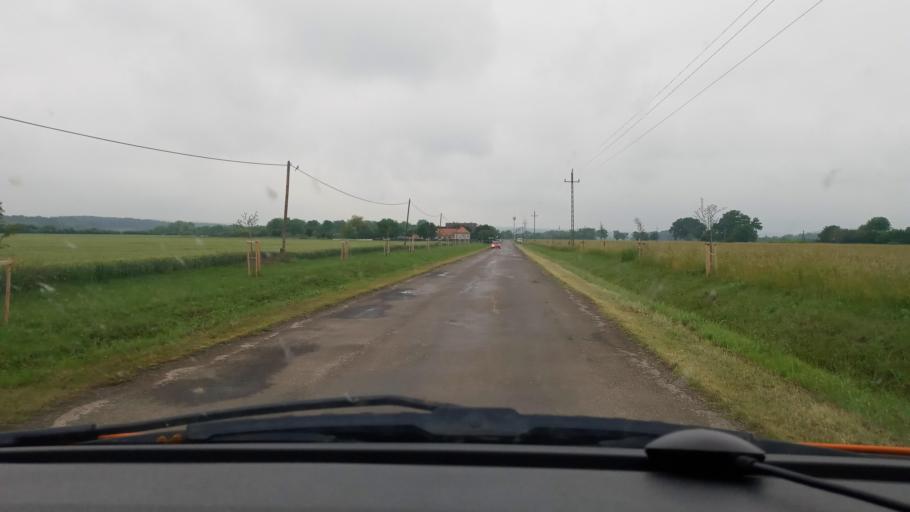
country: HU
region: Baranya
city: Szentlorinc
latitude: 46.0435
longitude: 17.9682
